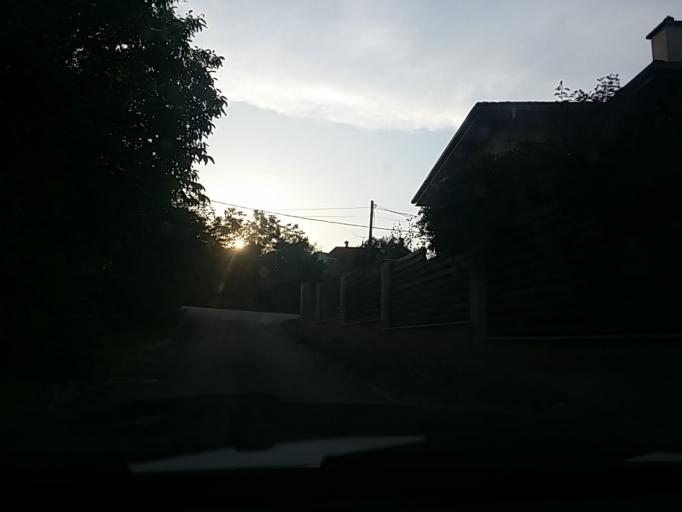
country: HU
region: Pest
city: Urom
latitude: 47.5811
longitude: 19.0248
